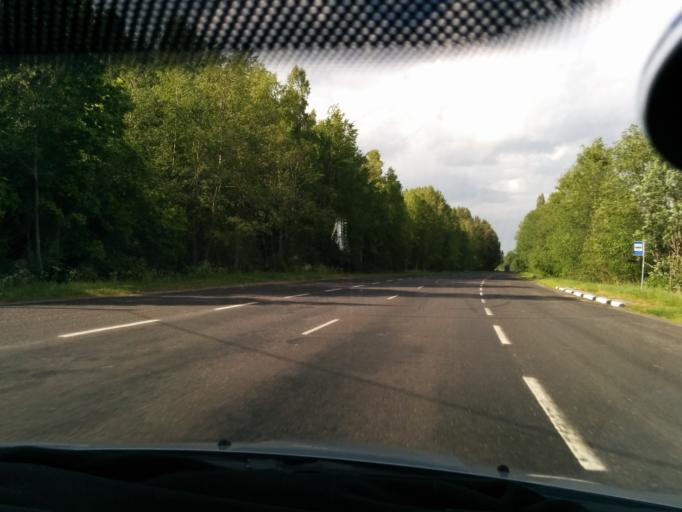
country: EE
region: Harju
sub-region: Loksa linn
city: Loksa
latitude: 59.5606
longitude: 25.7245
